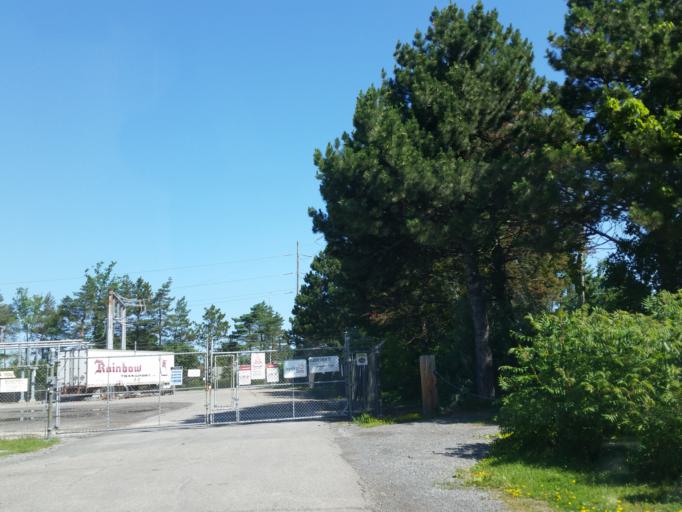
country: CA
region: Quebec
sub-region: Outaouais
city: Gatineau
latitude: 45.4661
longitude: -75.5494
